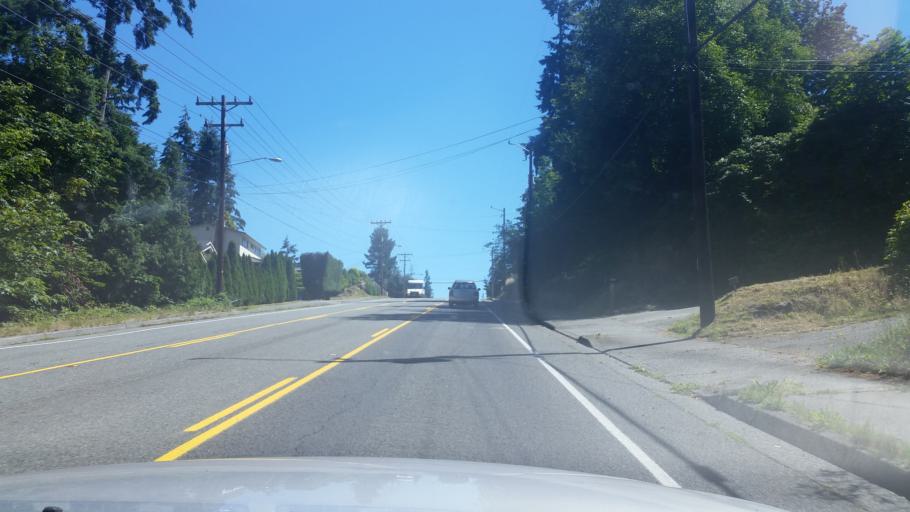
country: US
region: Washington
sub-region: Snohomish County
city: Esperance
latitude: 47.7777
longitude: -122.3579
